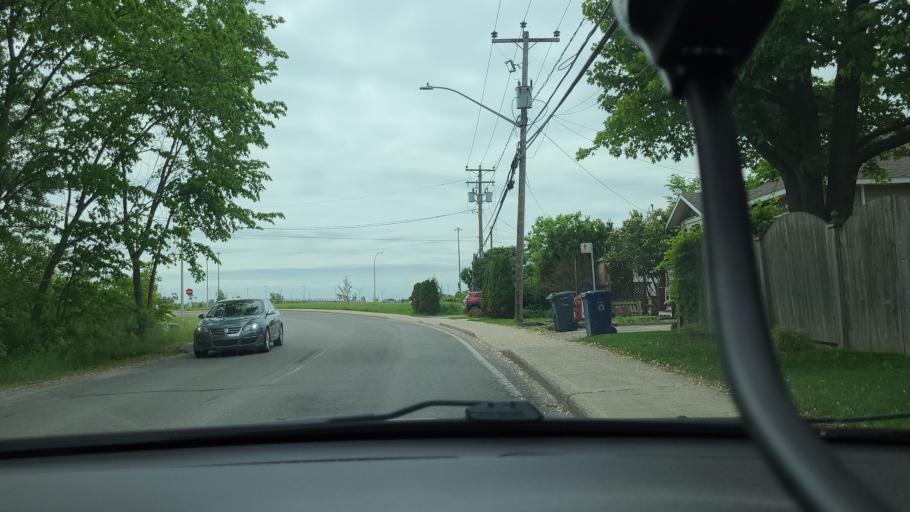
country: CA
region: Quebec
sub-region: Laurentides
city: Rosemere
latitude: 45.6023
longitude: -73.8028
